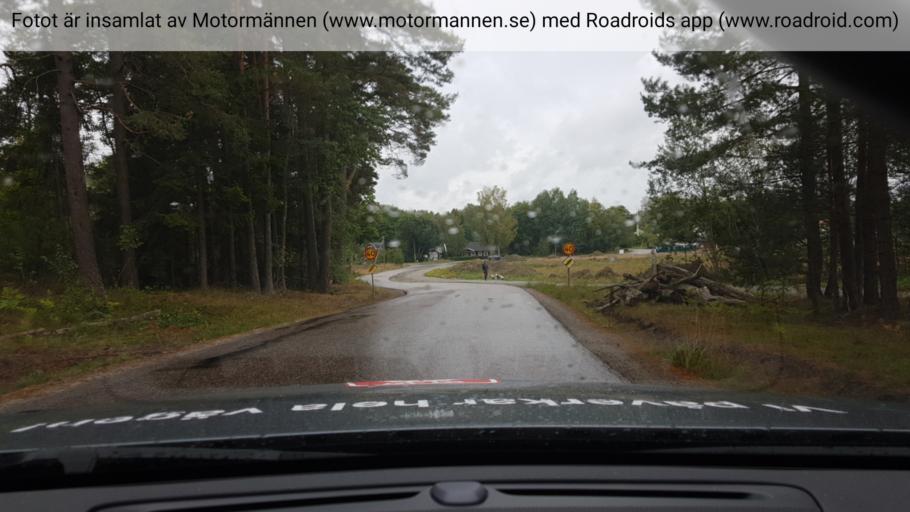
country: SE
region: Stockholm
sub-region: Nynashamns Kommun
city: Osmo
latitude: 59.0555
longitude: 17.8711
